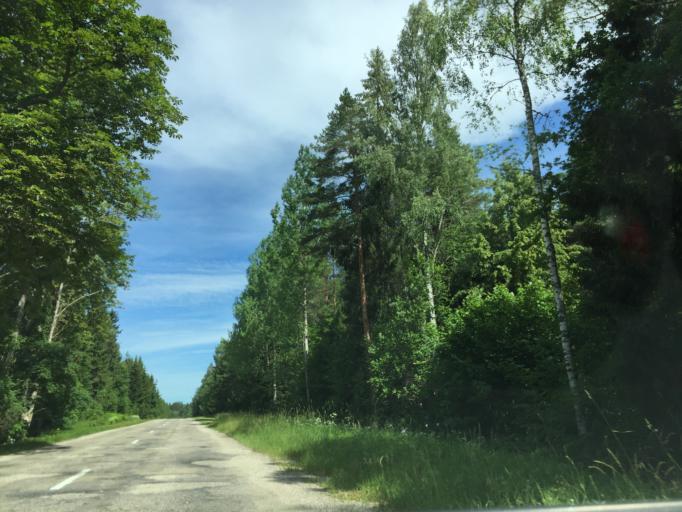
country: LV
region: Dundaga
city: Dundaga
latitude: 57.5731
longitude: 22.3059
